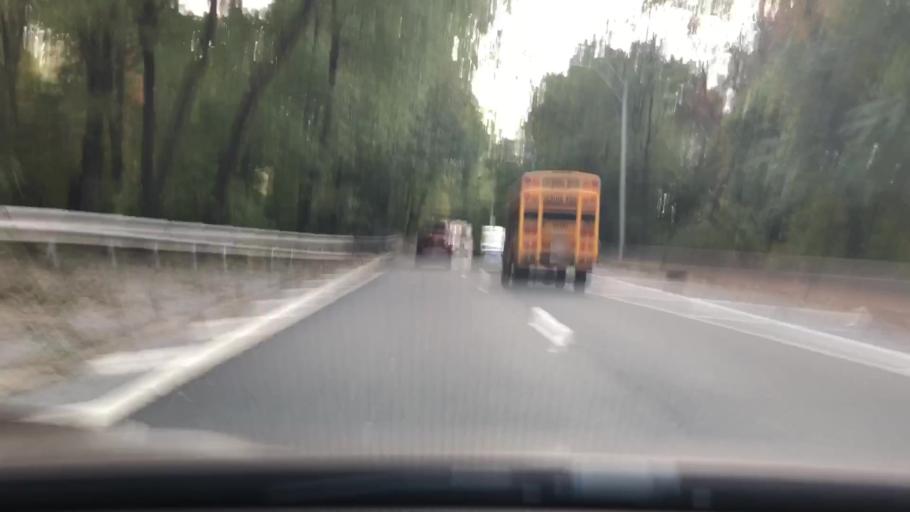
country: US
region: New Jersey
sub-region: Bergen County
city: Fort Lee
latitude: 40.8469
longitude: -73.9452
